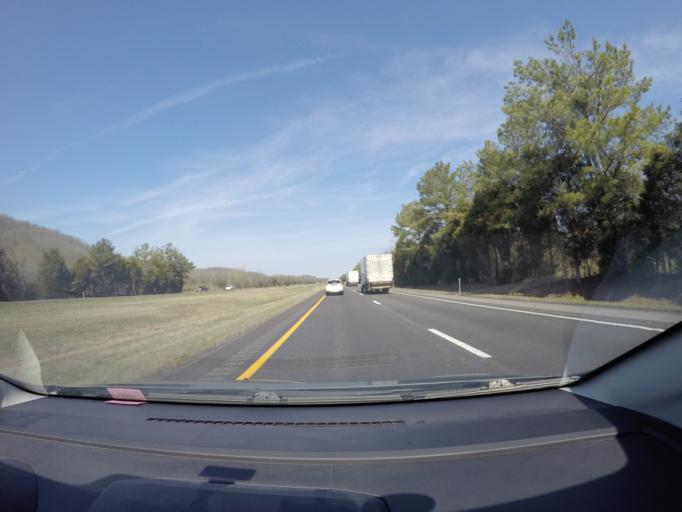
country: US
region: Tennessee
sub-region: Rutherford County
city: Plainview
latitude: 35.6517
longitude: -86.2581
